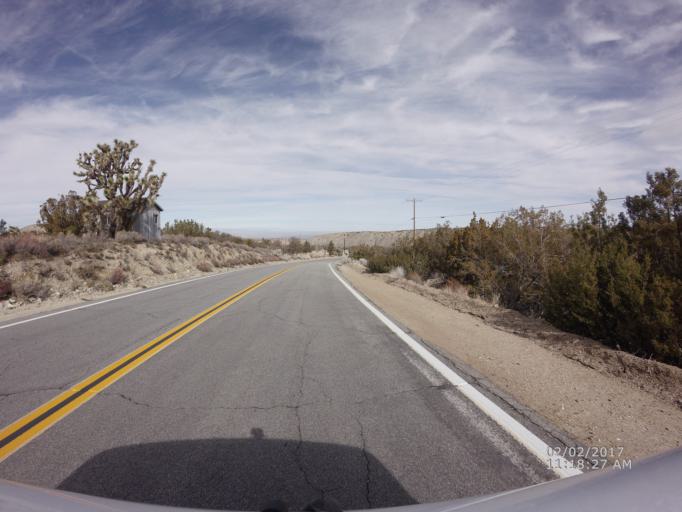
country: US
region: California
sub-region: Los Angeles County
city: Littlerock
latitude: 34.4352
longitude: -117.8969
